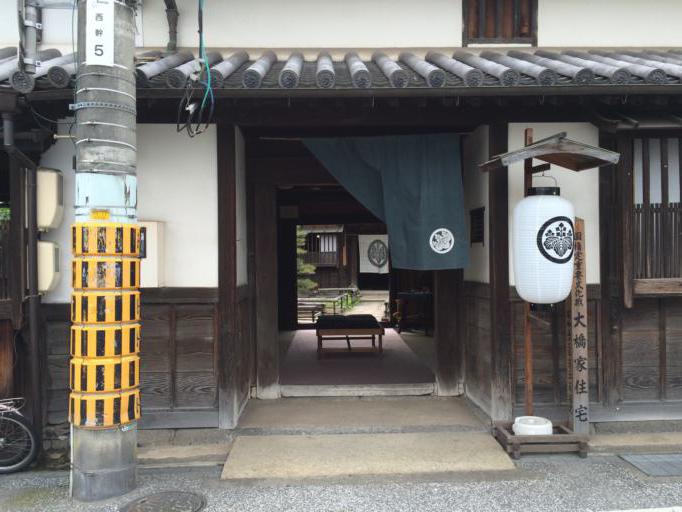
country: JP
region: Okayama
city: Kurashiki
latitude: 34.5973
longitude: 133.7683
